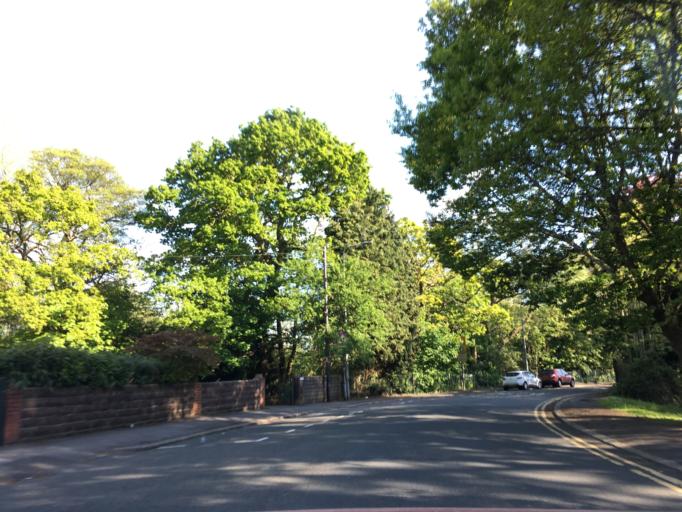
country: GB
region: Wales
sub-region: Cardiff
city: Cardiff
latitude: 51.5185
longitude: -3.1769
